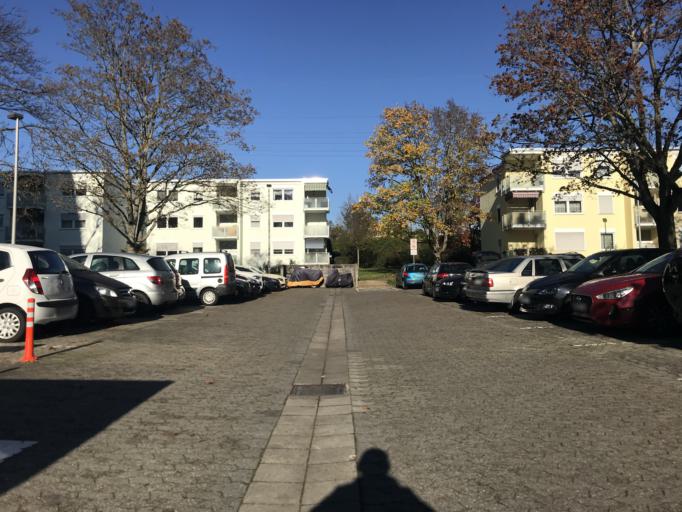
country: DE
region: Hesse
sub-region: Regierungsbezirk Darmstadt
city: Wiesbaden
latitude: 50.0512
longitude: 8.2459
